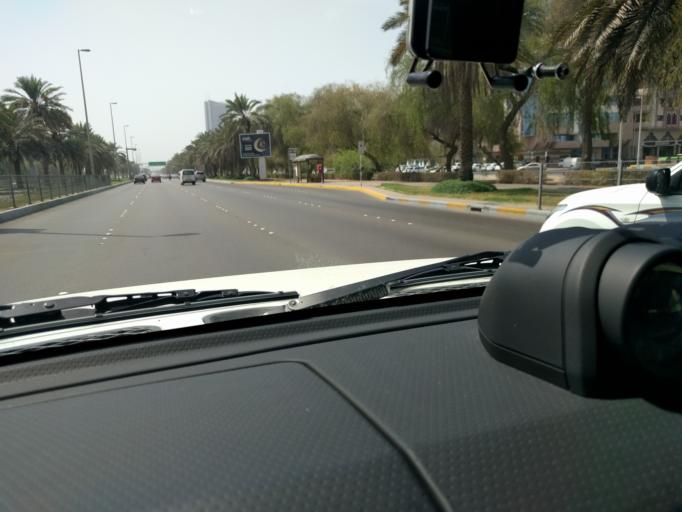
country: AE
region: Abu Dhabi
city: Abu Dhabi
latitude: 24.4467
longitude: 54.4012
